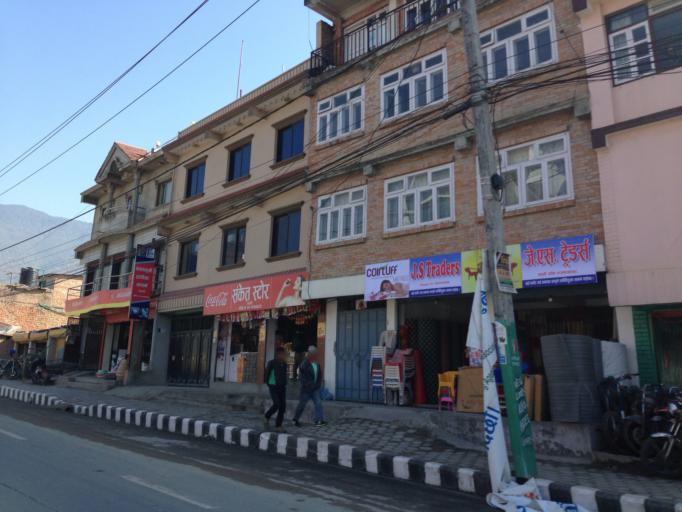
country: NP
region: Central Region
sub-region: Bagmati Zone
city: Kathmandu
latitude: 27.7685
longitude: 85.3566
